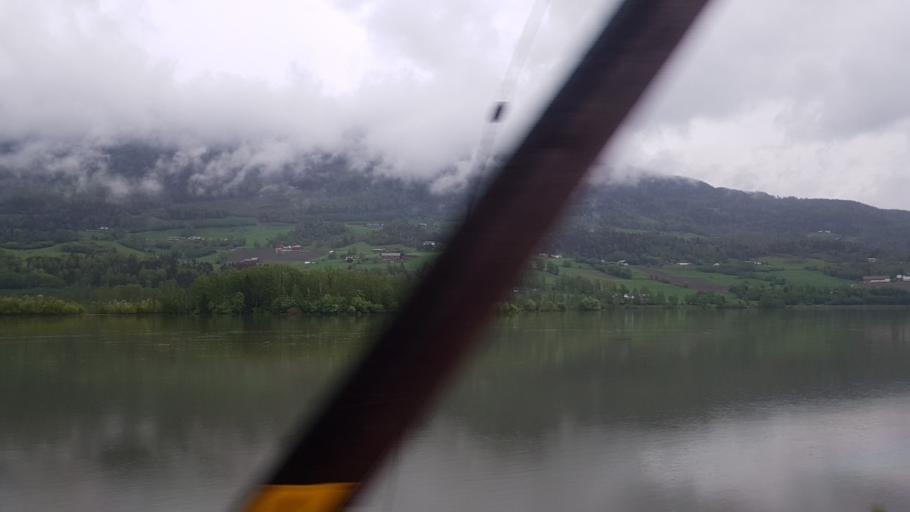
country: NO
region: Oppland
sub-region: Ringebu
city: Ringebu
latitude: 61.4562
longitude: 10.2028
